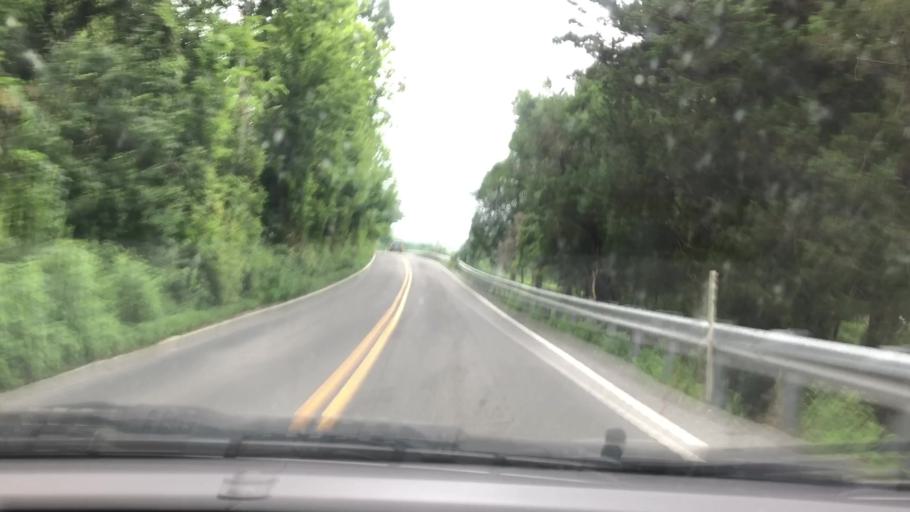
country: US
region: Tennessee
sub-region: Maury County
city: Spring Hill
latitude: 35.7985
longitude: -86.9997
